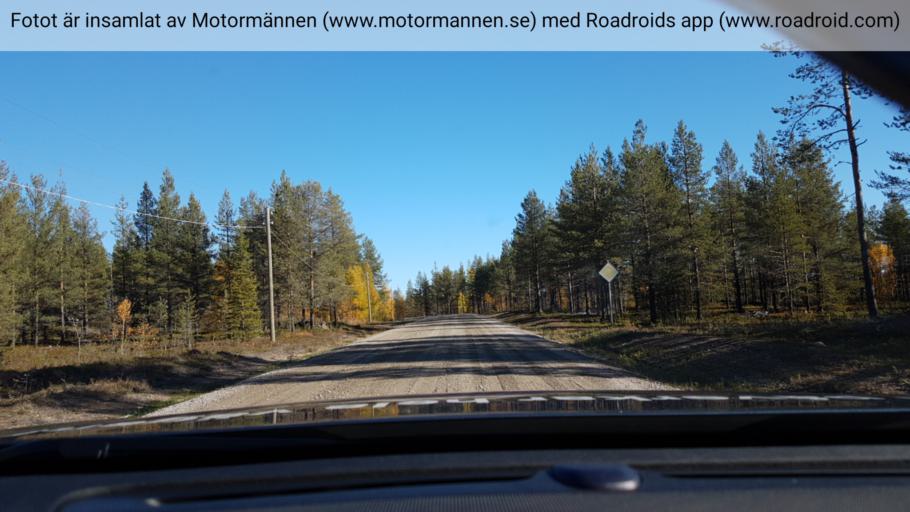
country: SE
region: Norrbotten
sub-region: Gallivare Kommun
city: Gaellivare
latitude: 66.7482
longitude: 20.9329
